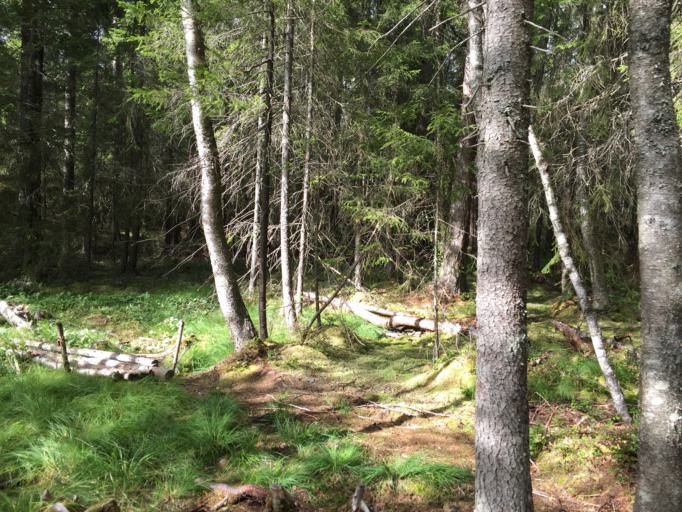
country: NO
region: Akershus
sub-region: Raelingen
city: Fjerdingby
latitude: 59.9076
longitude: 11.0337
